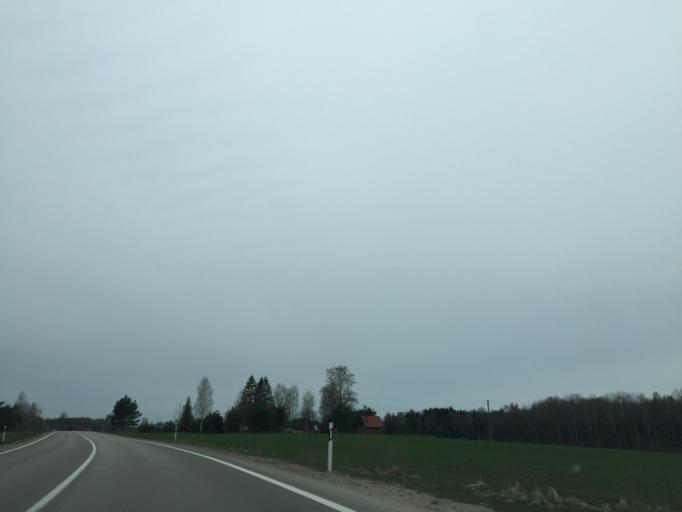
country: LV
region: Rezekne
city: Rezekne
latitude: 56.5153
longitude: 27.4659
